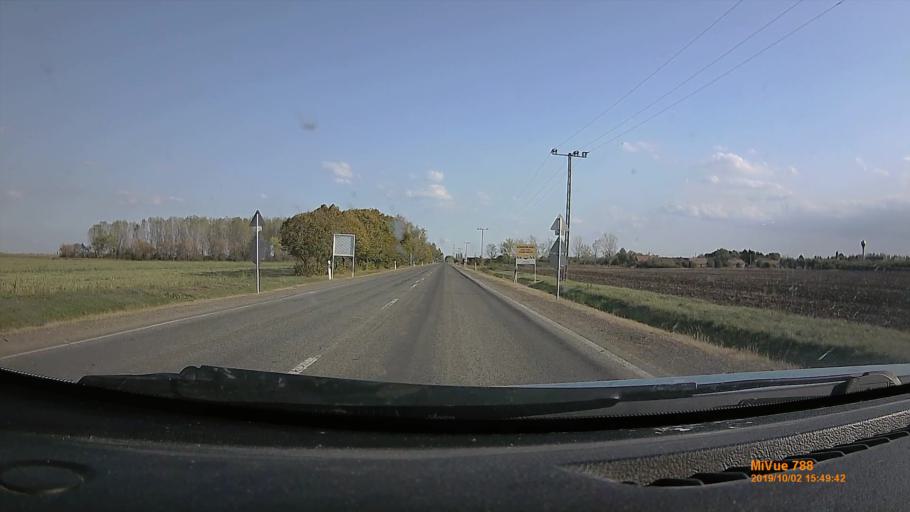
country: HU
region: Heves
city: Kerecsend
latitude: 47.7719
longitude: 20.3795
